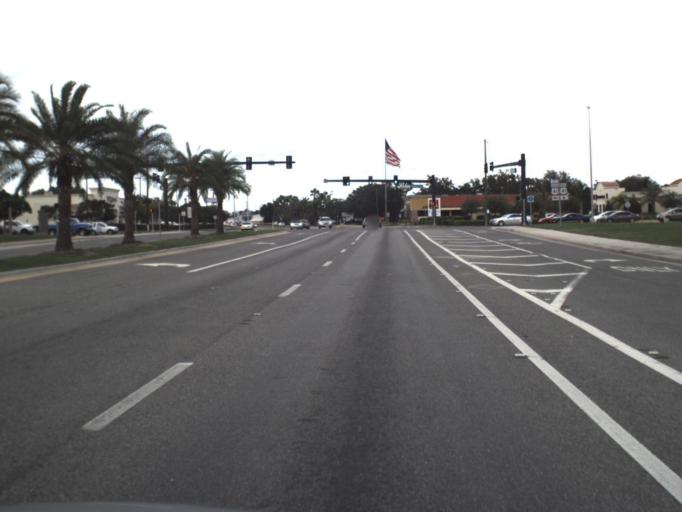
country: US
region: Florida
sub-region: Sarasota County
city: Venice Gardens
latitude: 27.0780
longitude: -82.4248
